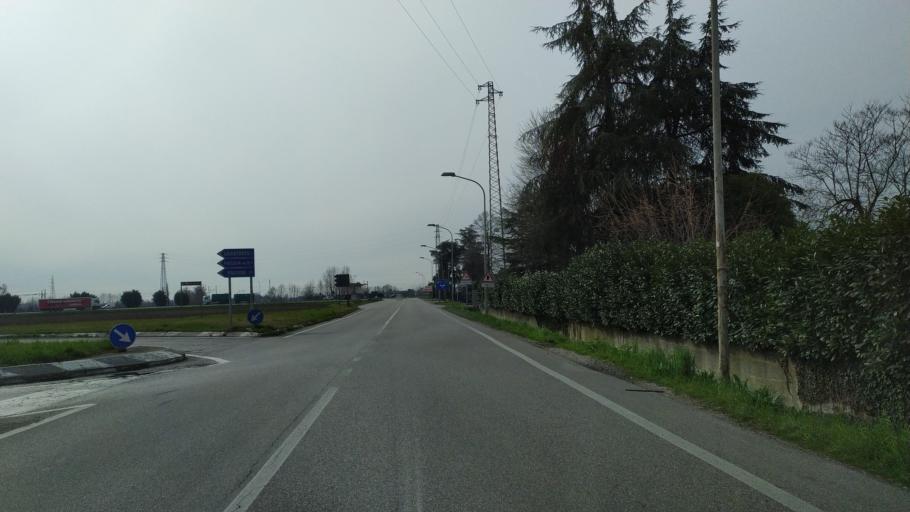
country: IT
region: Veneto
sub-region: Provincia di Padova
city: Carmignano di Brenta
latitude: 45.6182
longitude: 11.6975
